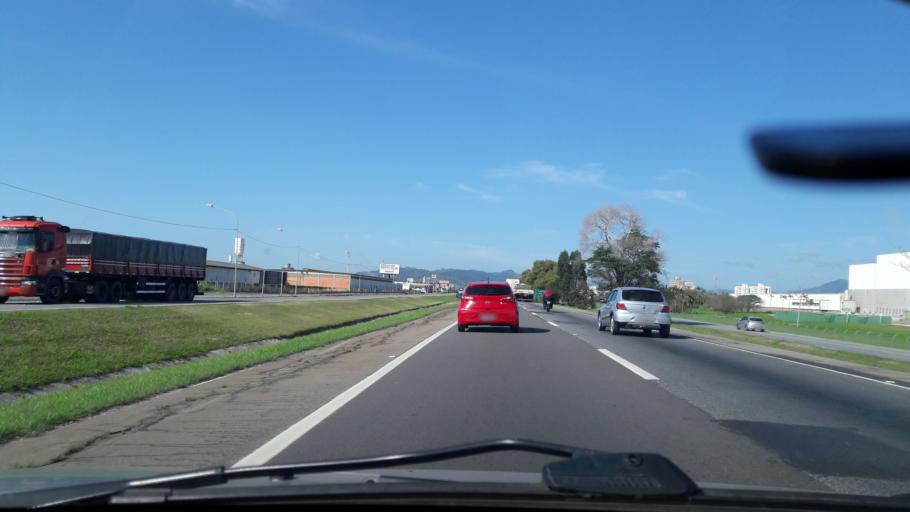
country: BR
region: Santa Catarina
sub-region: Tijucas
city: Tijucas
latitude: -27.2247
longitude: -48.6276
